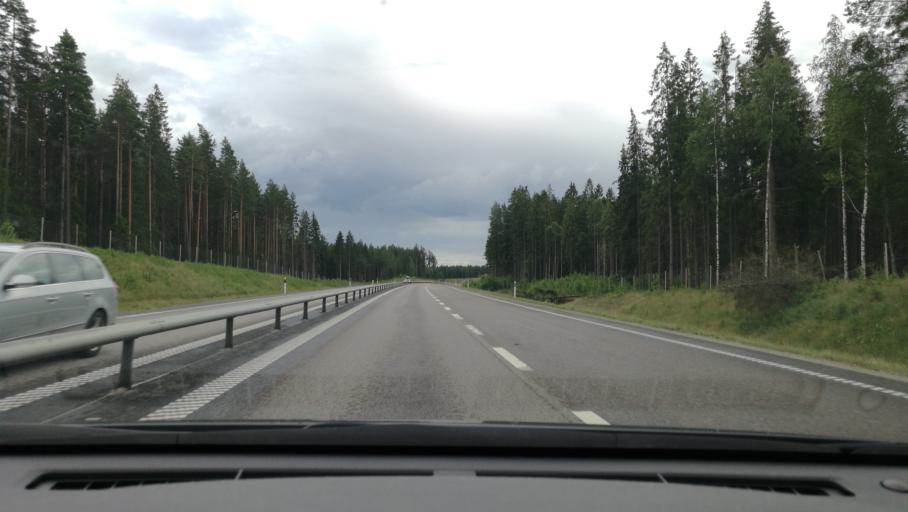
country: SE
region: Soedermanland
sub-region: Katrineholms Kommun
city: Katrineholm
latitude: 58.9915
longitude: 16.2620
